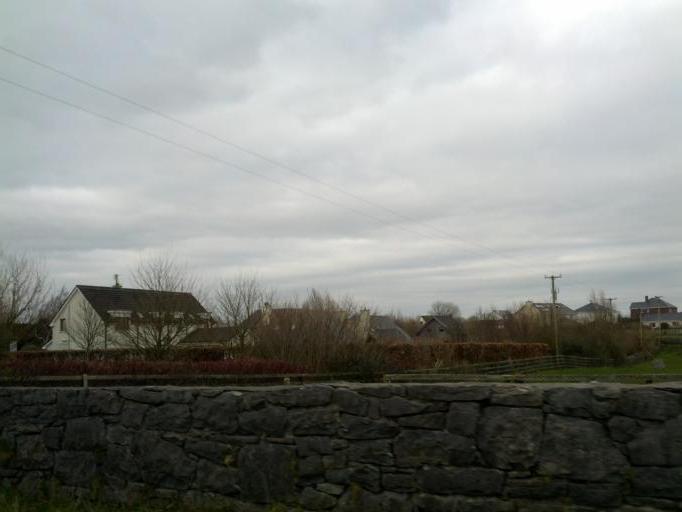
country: IE
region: Connaught
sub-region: County Galway
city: Oranmore
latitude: 53.2189
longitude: -8.8919
